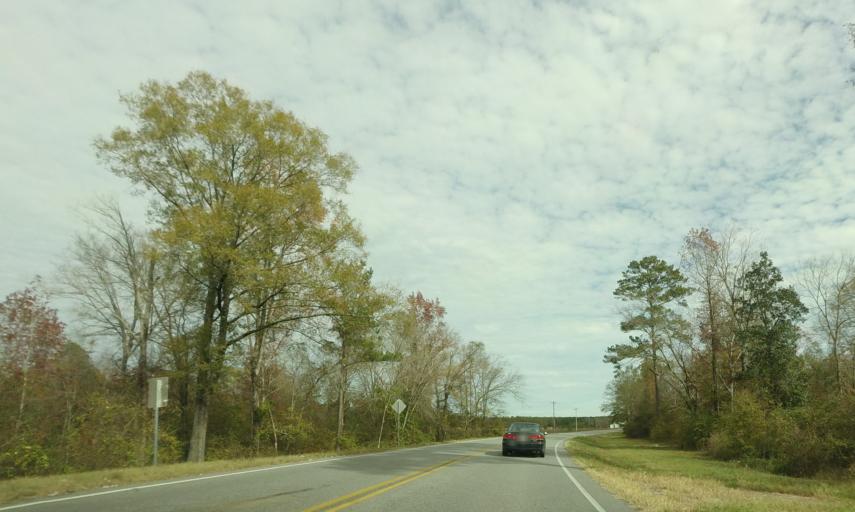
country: US
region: Georgia
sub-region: Bleckley County
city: Cochran
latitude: 32.4082
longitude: -83.2564
